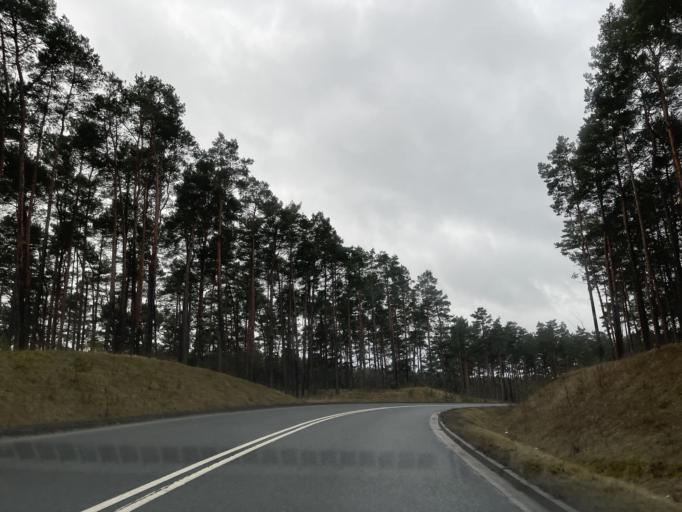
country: PL
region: Kujawsko-Pomorskie
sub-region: Powiat bydgoski
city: Nowa Wies Wielka
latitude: 53.0627
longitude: 18.0884
